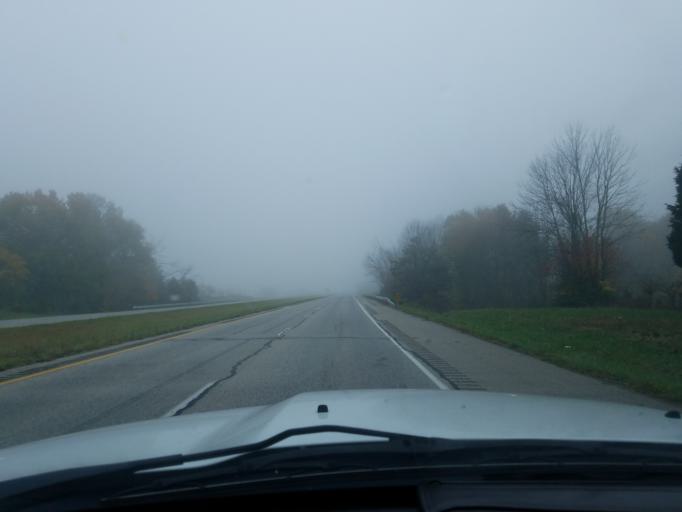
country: US
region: Indiana
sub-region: Floyd County
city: Galena
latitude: 38.3316
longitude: -85.8982
